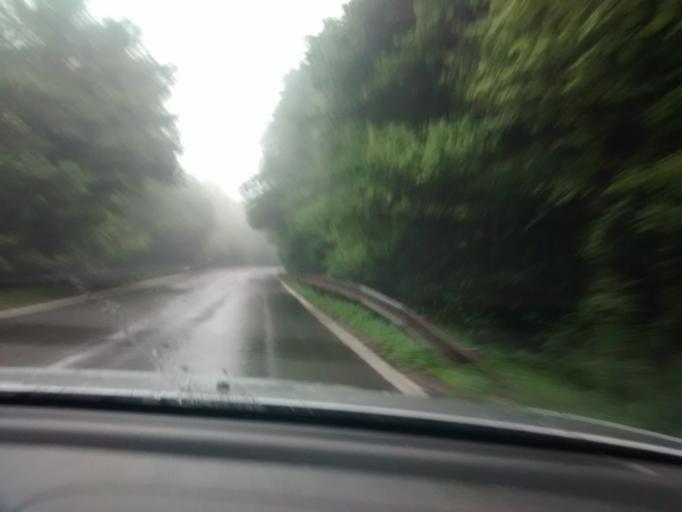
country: SK
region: Nitriansky
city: Handlova
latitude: 48.6610
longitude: 18.7320
